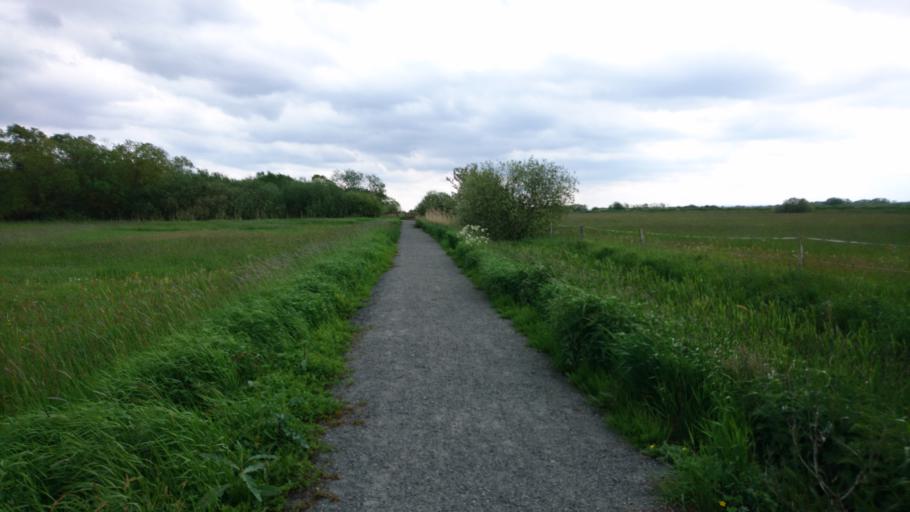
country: SE
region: Skane
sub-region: Kristianstads Kommun
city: Fjalkinge
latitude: 56.0044
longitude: 14.2412
